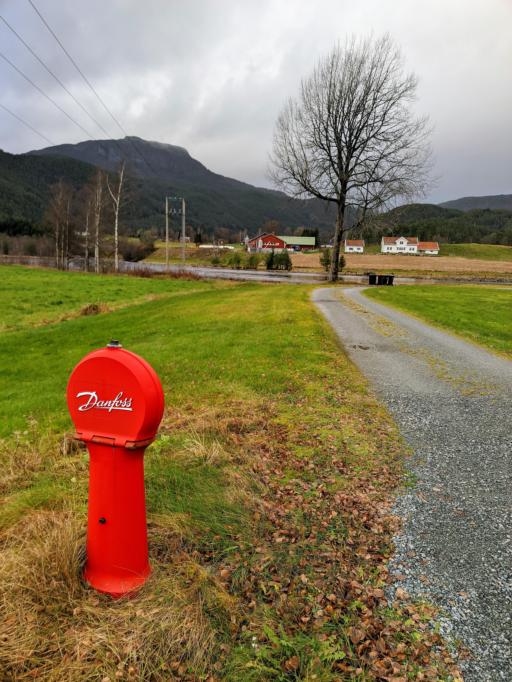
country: NO
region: Rogaland
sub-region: Suldal
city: Sand
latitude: 59.4619
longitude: 6.4235
